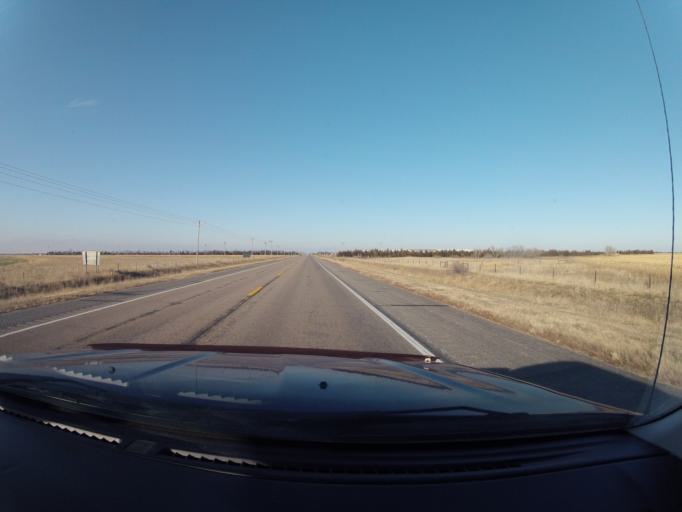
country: US
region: Nebraska
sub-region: Kearney County
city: Minden
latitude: 40.6243
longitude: -98.9515
